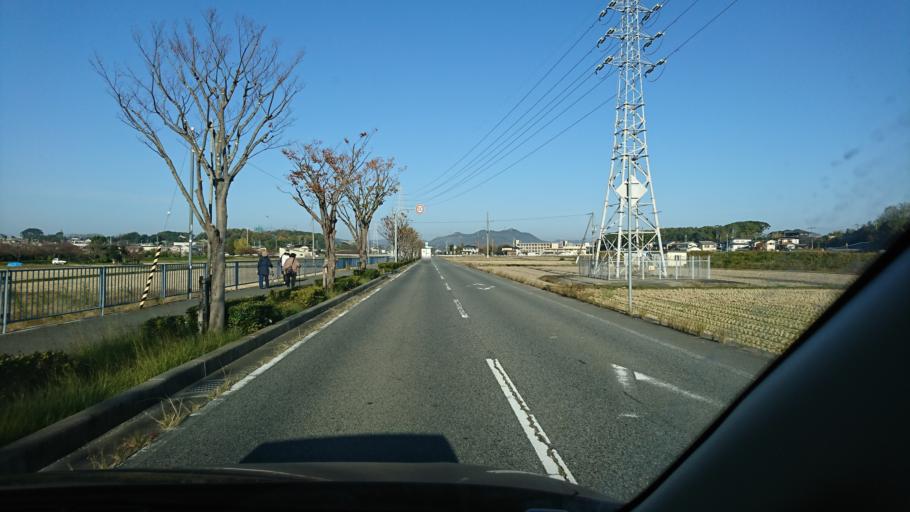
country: JP
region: Hyogo
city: Kakogawacho-honmachi
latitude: 34.7712
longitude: 134.8815
